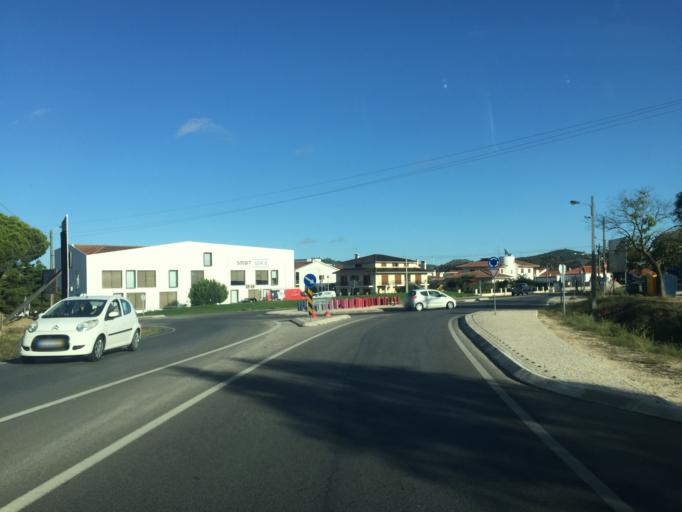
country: PT
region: Lisbon
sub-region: Torres Vedras
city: Torres Vedras
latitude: 39.1064
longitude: -9.2596
